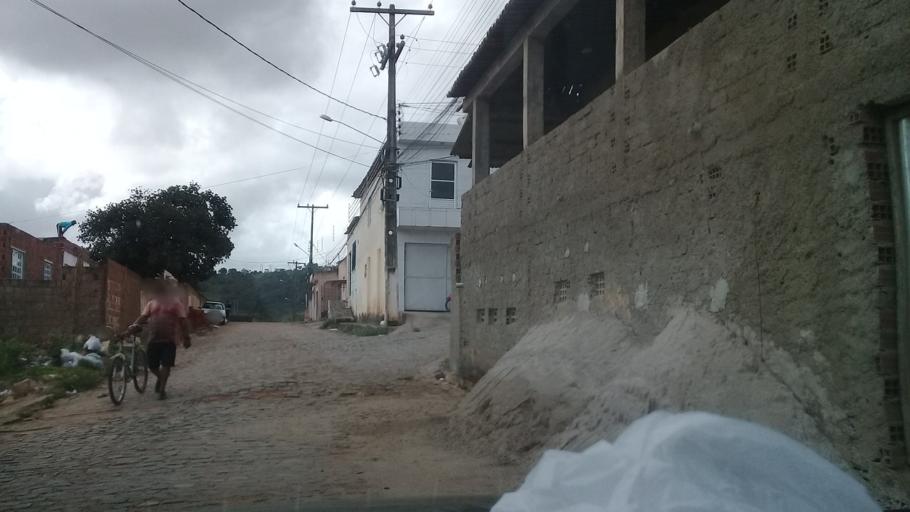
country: BR
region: Pernambuco
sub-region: Vitoria De Santo Antao
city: Vitoria de Santo Antao
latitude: -8.1317
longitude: -35.2951
